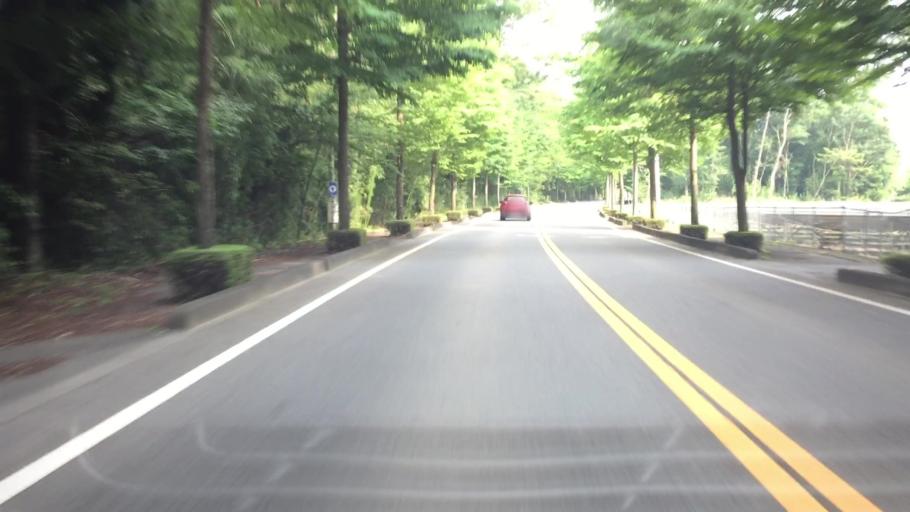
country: JP
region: Tochigi
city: Kuroiso
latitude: 36.9768
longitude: 139.9686
